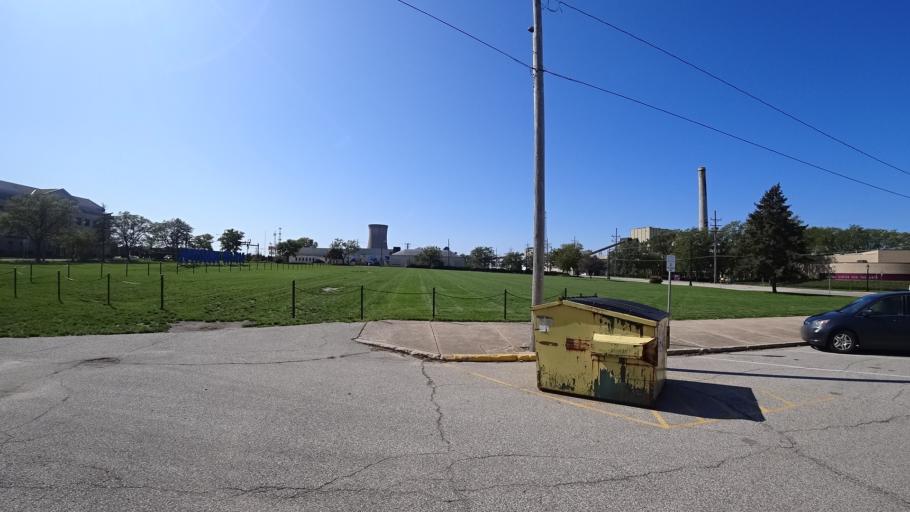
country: US
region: Indiana
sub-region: LaPorte County
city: Michigan City
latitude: 41.7202
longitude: -86.9032
